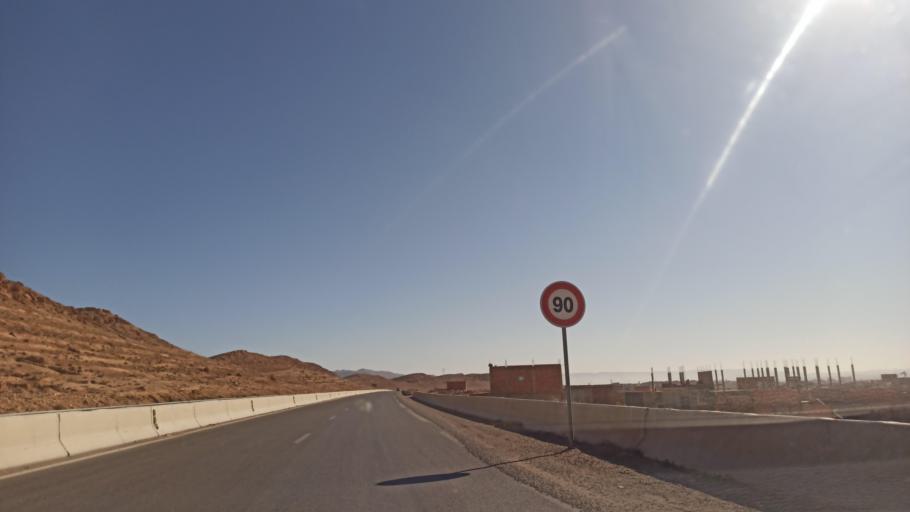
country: TN
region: Gafsa
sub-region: Gafsa Municipality
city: Gafsa
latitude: 34.4510
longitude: 8.7804
